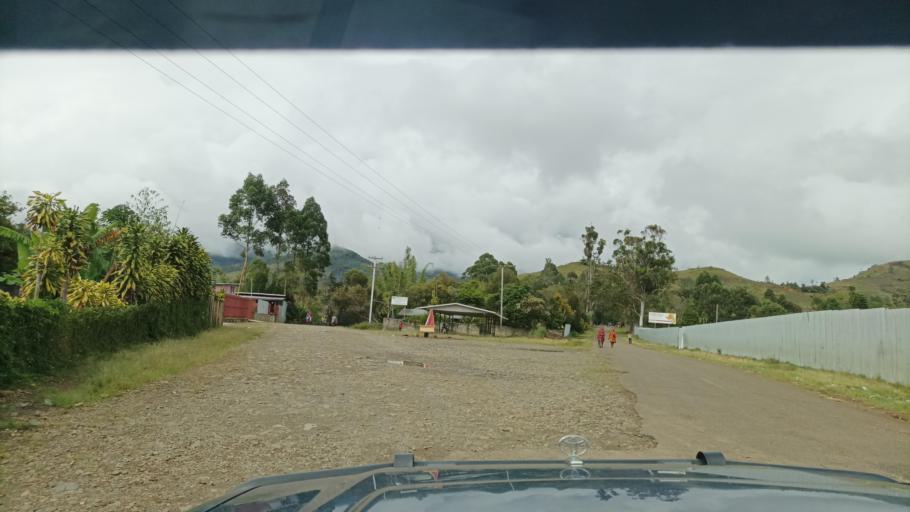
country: PG
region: Jiwaka
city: Minj
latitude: -5.9111
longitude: 144.6876
